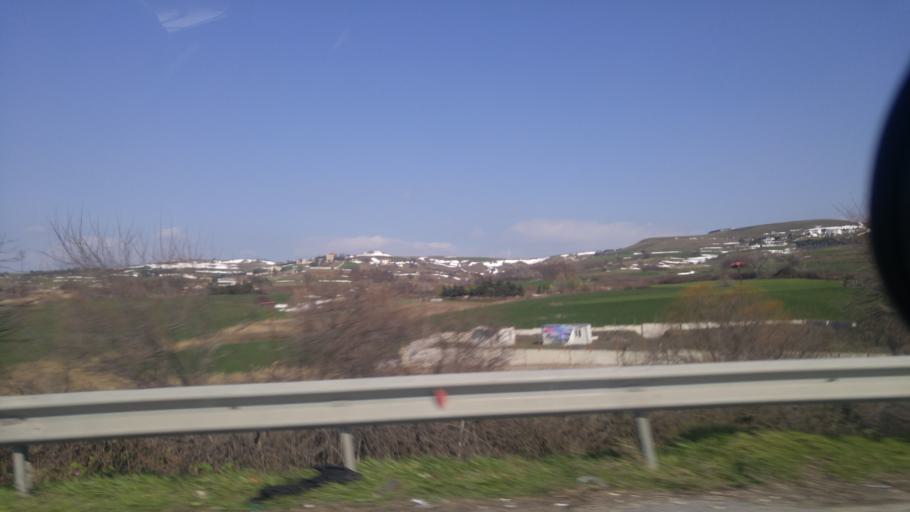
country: TR
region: Istanbul
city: Celaliye
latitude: 41.0640
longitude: 28.4051
